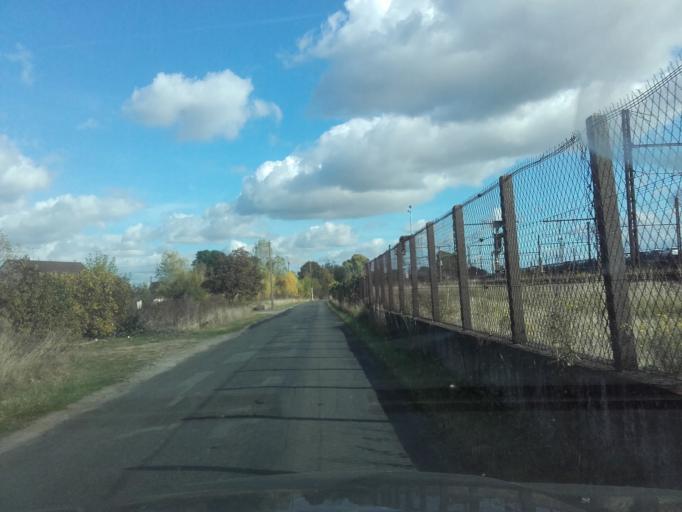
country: FR
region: Centre
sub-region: Departement d'Indre-et-Loire
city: Saint-Pierre-des-Corps
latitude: 47.3925
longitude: 0.7537
